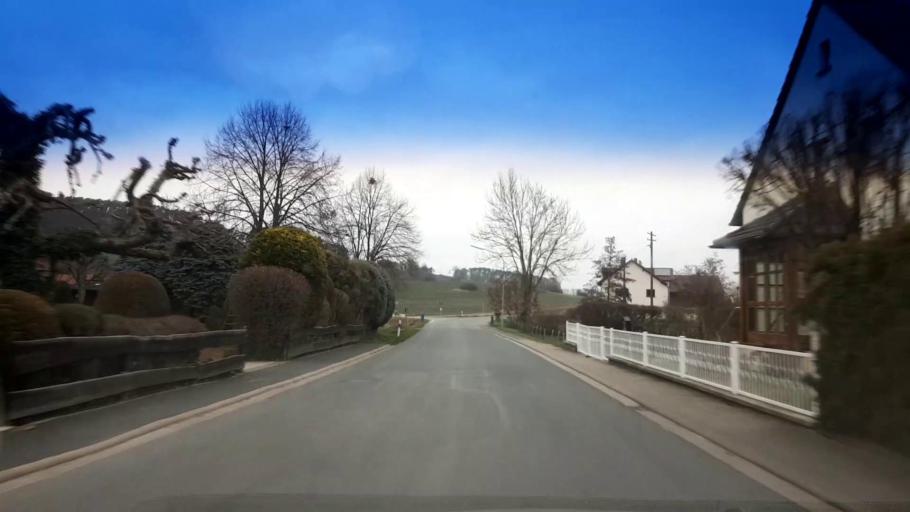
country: DE
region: Bavaria
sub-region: Upper Franconia
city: Hallerndorf
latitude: 49.7629
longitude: 10.9858
